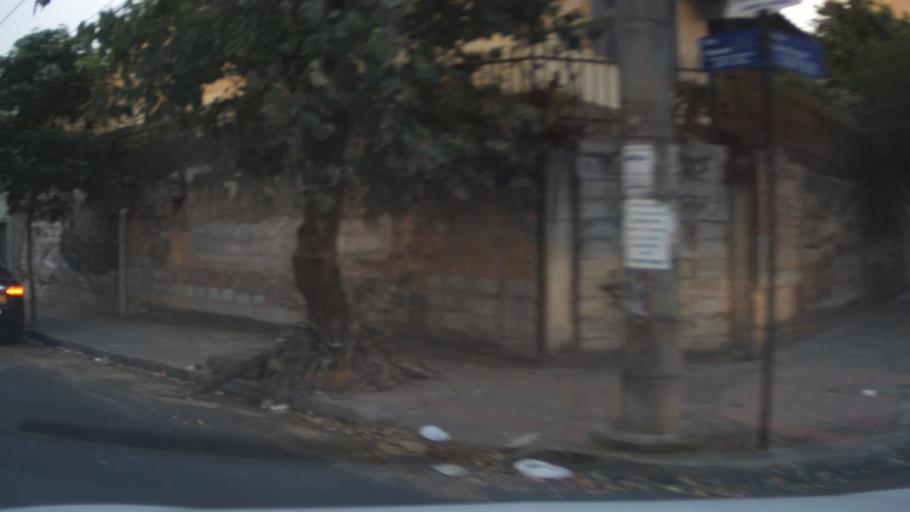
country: BR
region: Minas Gerais
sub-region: Belo Horizonte
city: Belo Horizonte
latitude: -19.8929
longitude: -43.9322
